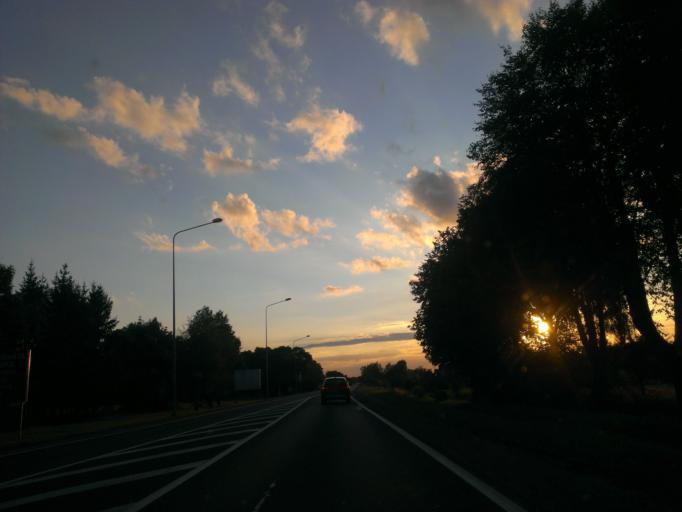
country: LV
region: Sigulda
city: Sigulda
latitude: 57.1418
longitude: 24.8403
